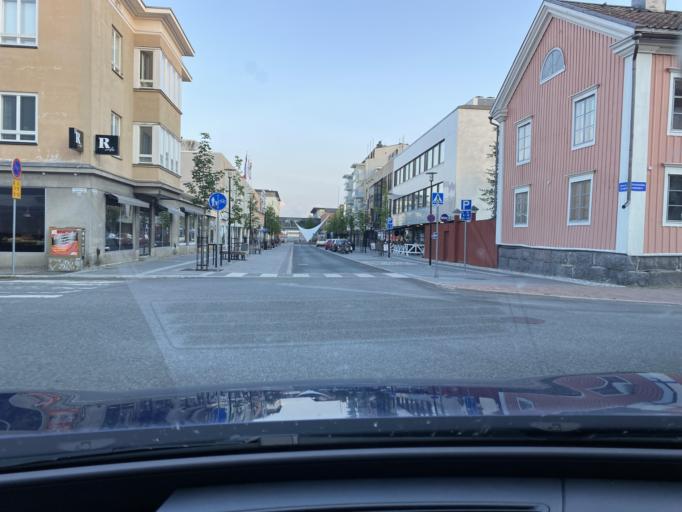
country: FI
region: Central Ostrobothnia
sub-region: Kokkola
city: Kokkola
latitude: 63.8376
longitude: 23.1325
